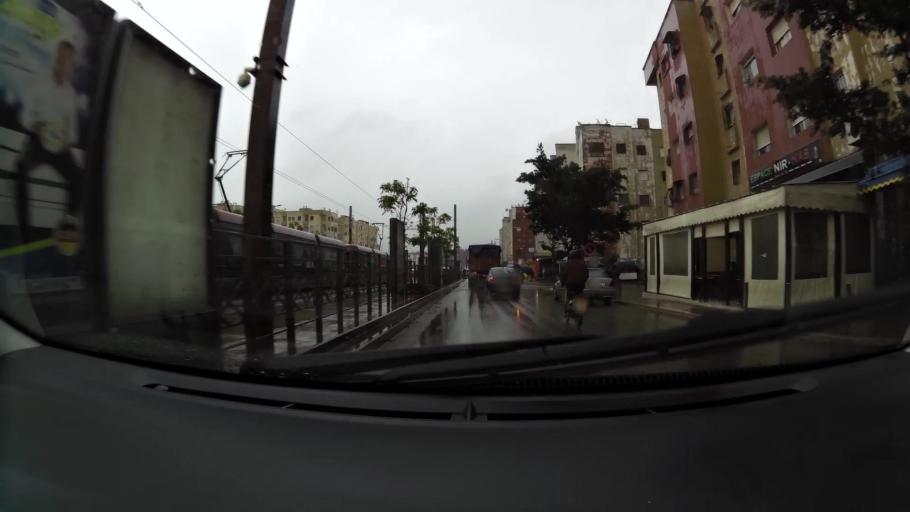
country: MA
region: Grand Casablanca
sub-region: Mediouna
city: Tit Mellil
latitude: 33.5867
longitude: -7.5020
